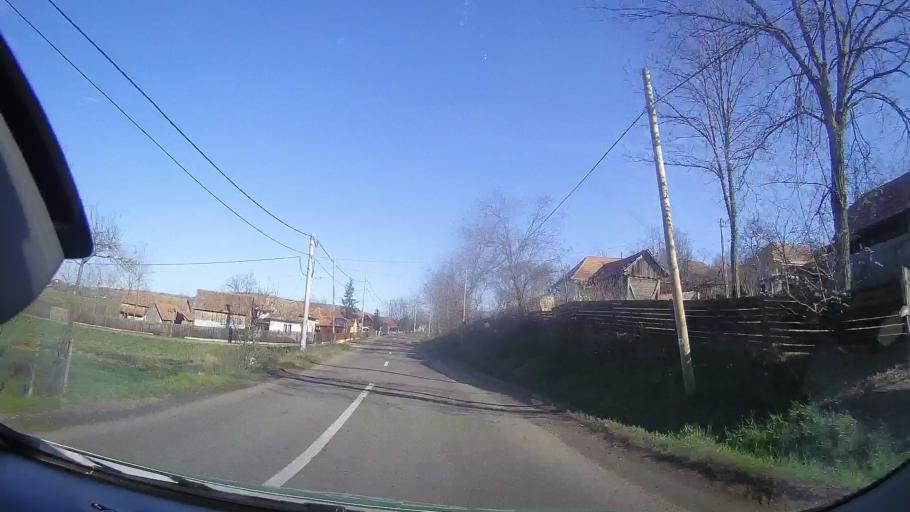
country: RO
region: Mures
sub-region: Comuna Band
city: Band
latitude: 46.5786
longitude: 24.3526
